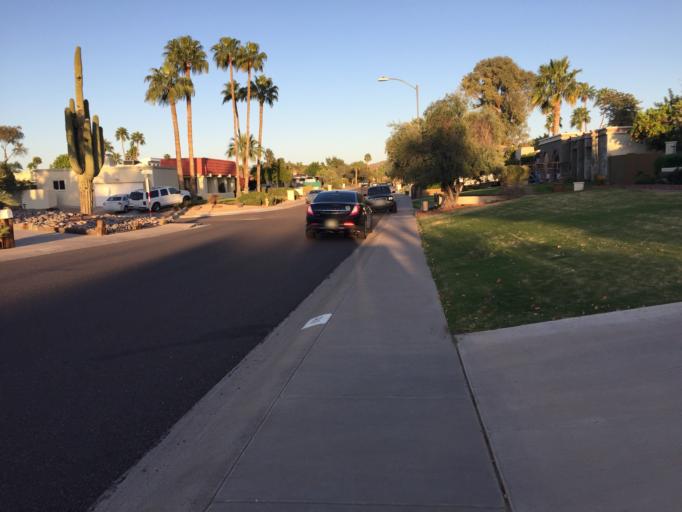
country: US
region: Arizona
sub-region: Maricopa County
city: Paradise Valley
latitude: 33.5684
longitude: -112.0121
